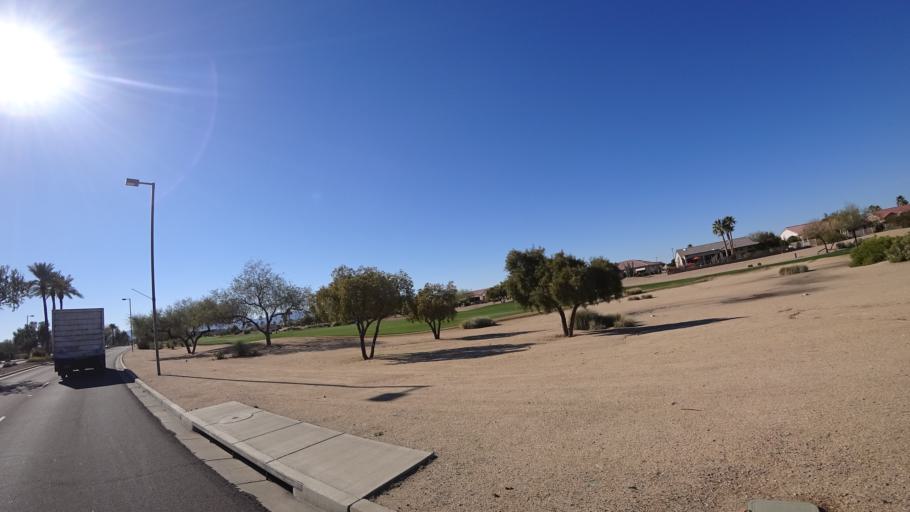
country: US
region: Arizona
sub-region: Maricopa County
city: Sun City West
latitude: 33.6650
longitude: -112.3943
